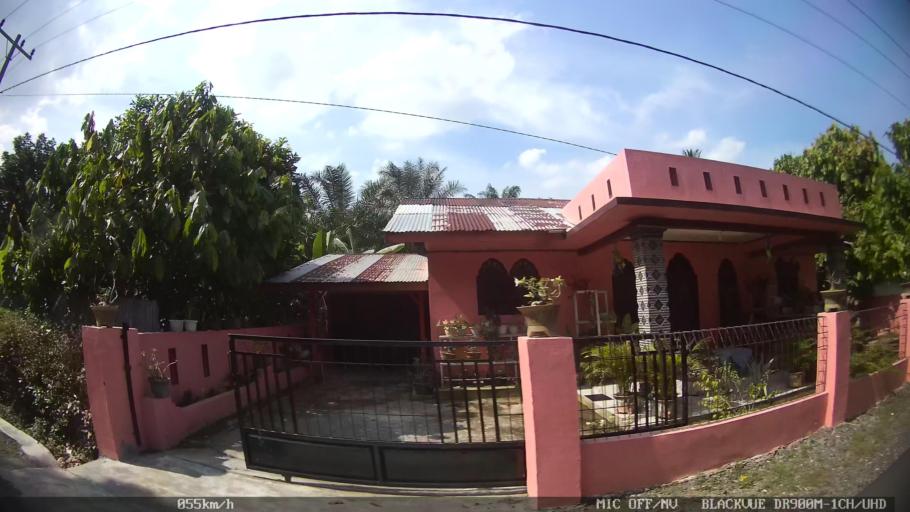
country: ID
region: North Sumatra
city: Binjai
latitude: 3.6345
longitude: 98.5223
